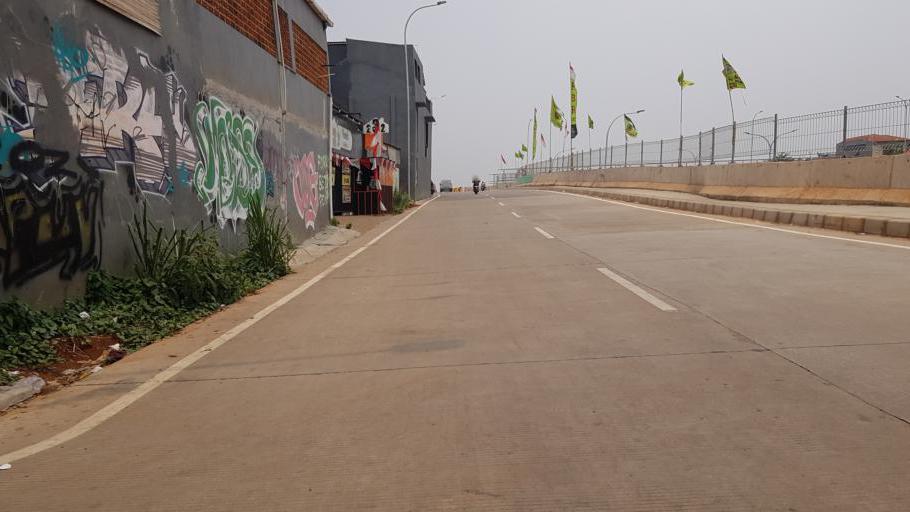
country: ID
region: West Java
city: Pamulang
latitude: -6.3307
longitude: 106.8006
